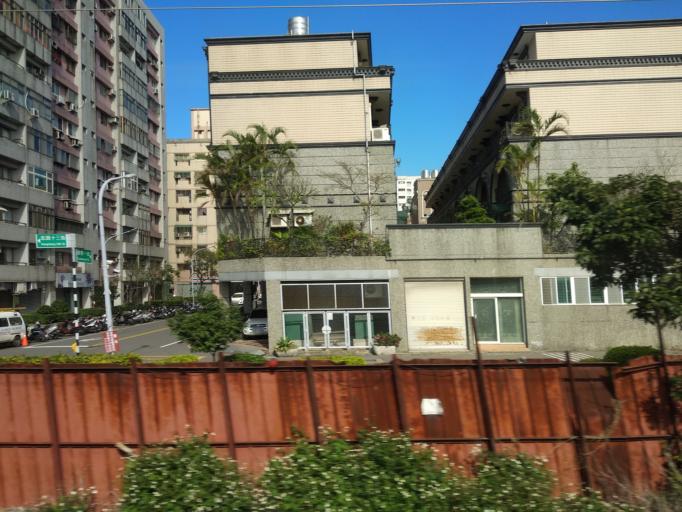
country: TW
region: Taiwan
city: Taoyuan City
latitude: 24.9839
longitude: 121.2888
